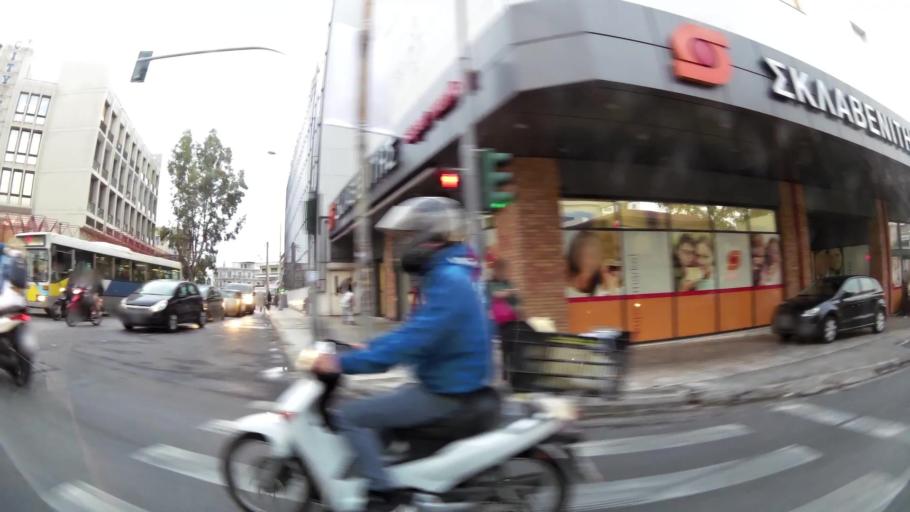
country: GR
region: Attica
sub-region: Nomarchia Athinas
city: Dhafni
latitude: 37.9489
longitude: 23.7384
